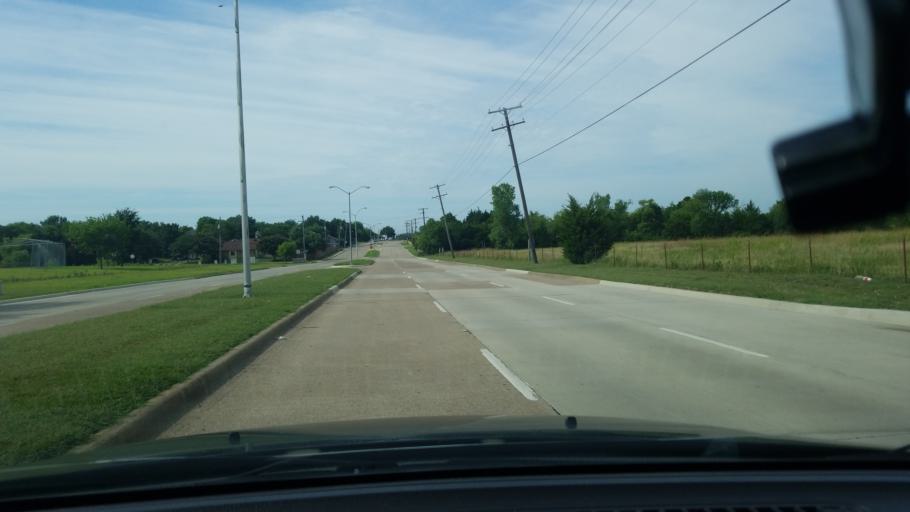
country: US
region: Texas
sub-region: Dallas County
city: Balch Springs
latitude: 32.7740
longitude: -96.6655
